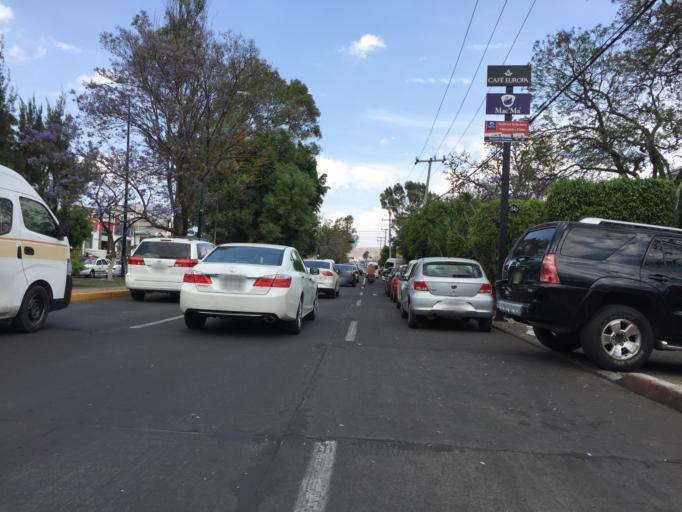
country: MX
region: Michoacan
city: Morelia
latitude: 19.6964
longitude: -101.1666
